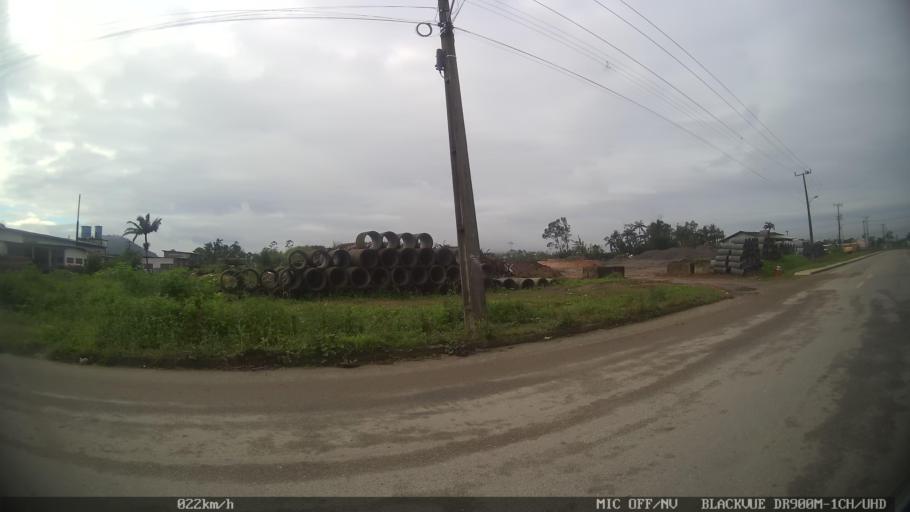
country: BR
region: Santa Catarina
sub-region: Joinville
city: Joinville
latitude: -26.0297
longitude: -48.8457
